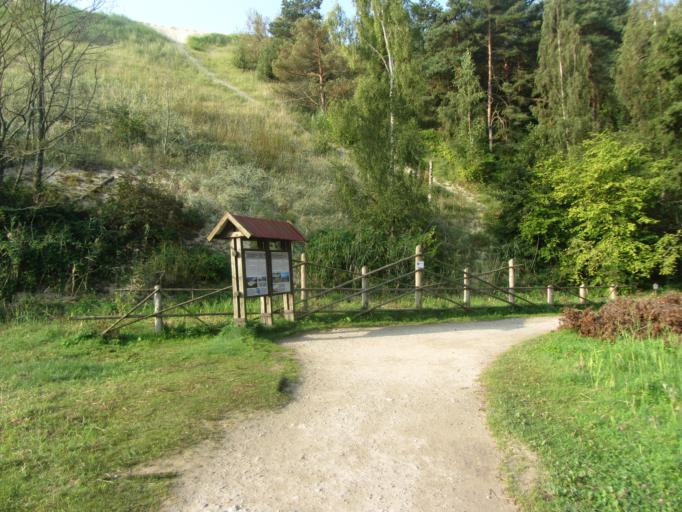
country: LT
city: Nida
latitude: 55.2959
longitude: 20.9950
